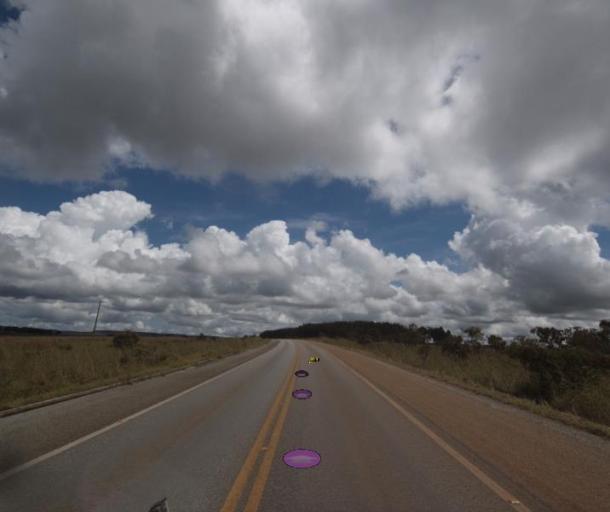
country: BR
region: Goias
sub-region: Pirenopolis
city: Pirenopolis
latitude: -15.7486
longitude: -48.6677
